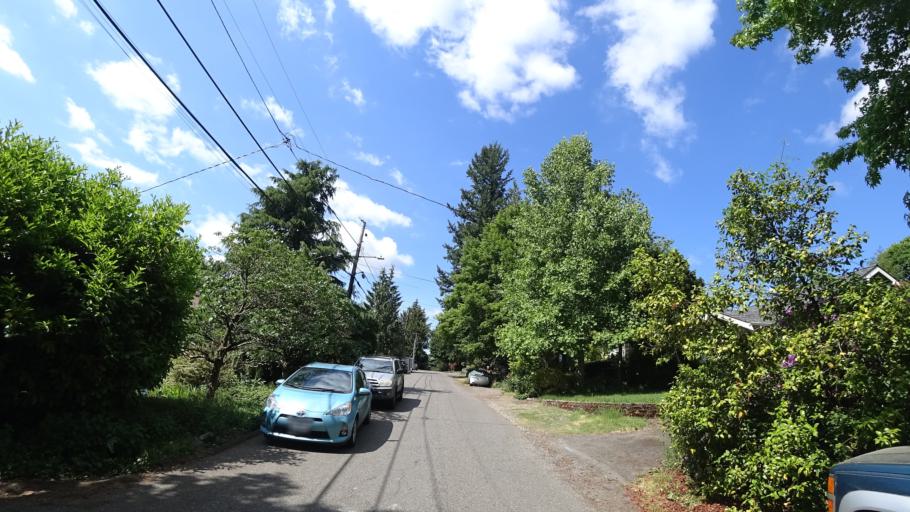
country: US
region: Oregon
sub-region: Washington County
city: Garden Home-Whitford
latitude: 45.4693
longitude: -122.7103
